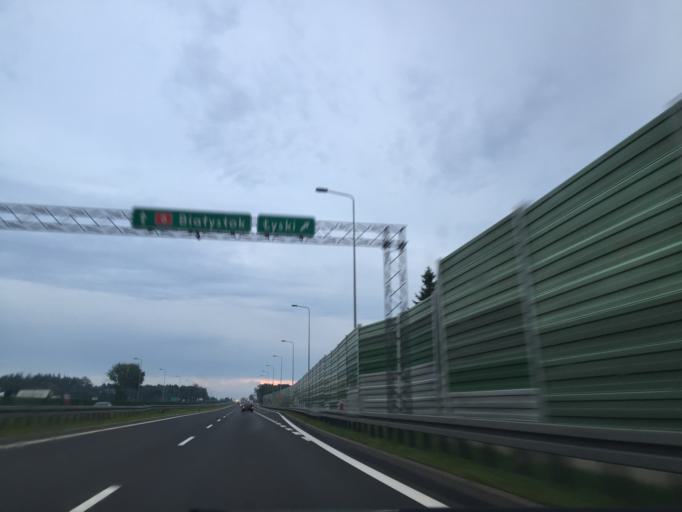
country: PL
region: Podlasie
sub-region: Powiat bialostocki
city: Choroszcz
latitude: 53.1525
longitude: 23.0368
